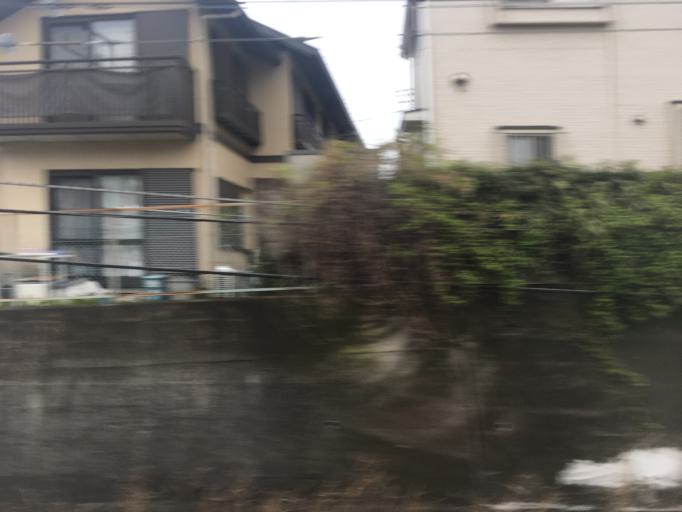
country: JP
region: Tokyo
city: Kokubunji
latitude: 35.7073
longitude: 139.4663
